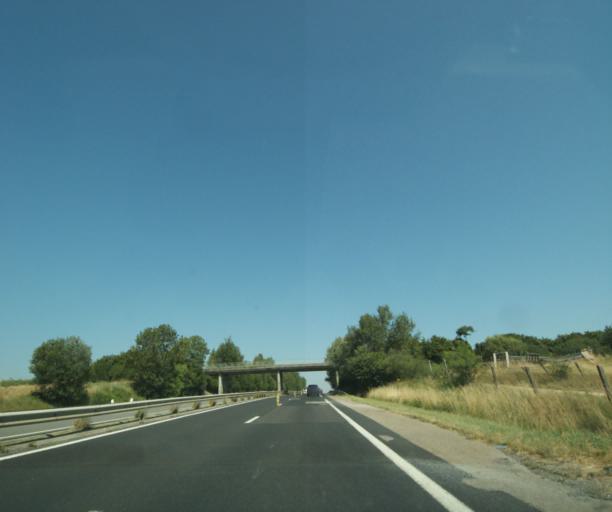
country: FR
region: Lorraine
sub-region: Departement de Meurthe-et-Moselle
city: Domgermain
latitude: 48.6557
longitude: 5.8427
